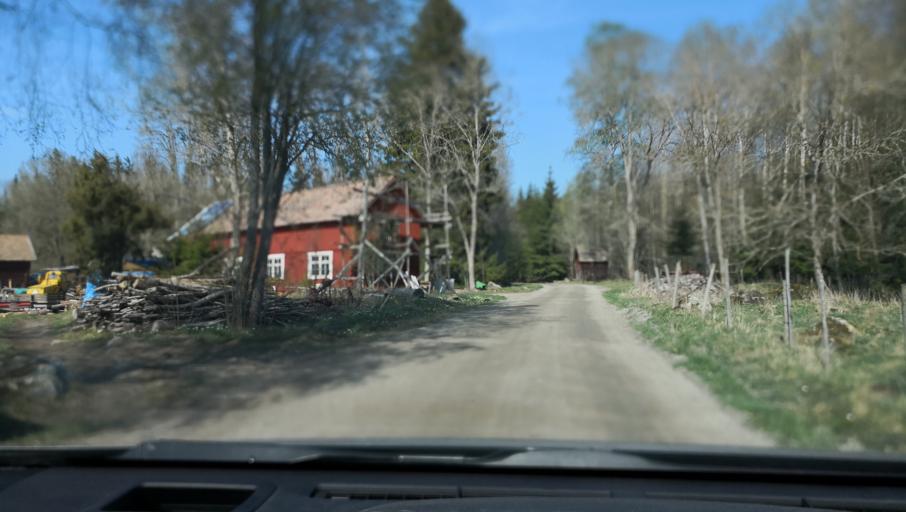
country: SE
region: Uppsala
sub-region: Heby Kommun
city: Heby
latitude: 60.0118
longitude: 16.7364
